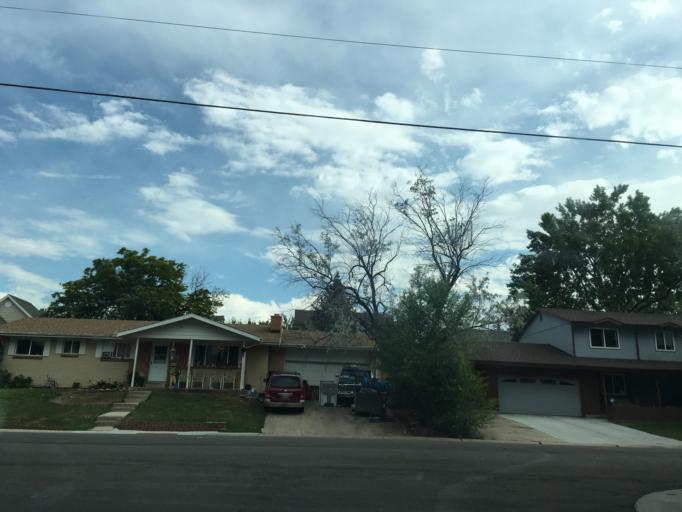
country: US
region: Colorado
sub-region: Jefferson County
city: Lakewood
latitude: 39.6757
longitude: -105.0601
